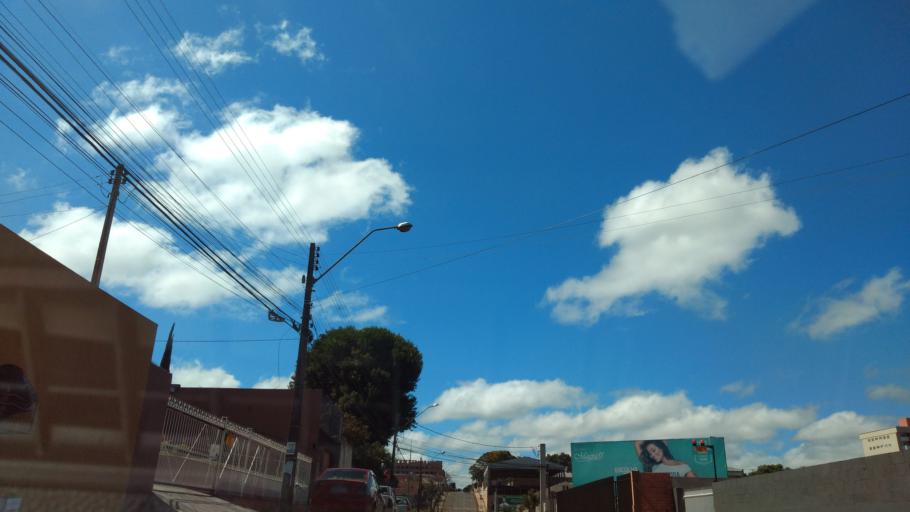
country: BR
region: Parana
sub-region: Guarapuava
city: Guarapuava
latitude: -25.3973
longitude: -51.4702
